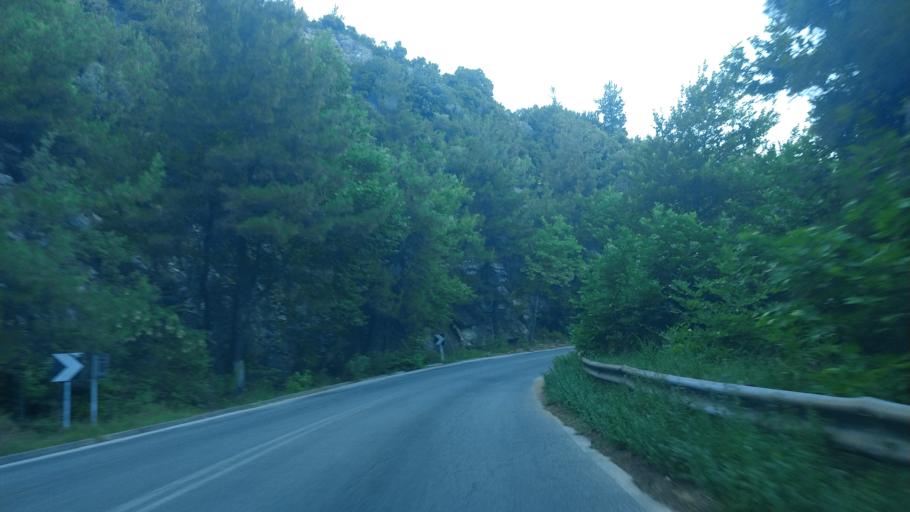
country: GR
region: East Macedonia and Thrace
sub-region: Nomos Kavalas
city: Potamia
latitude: 40.7252
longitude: 24.7324
